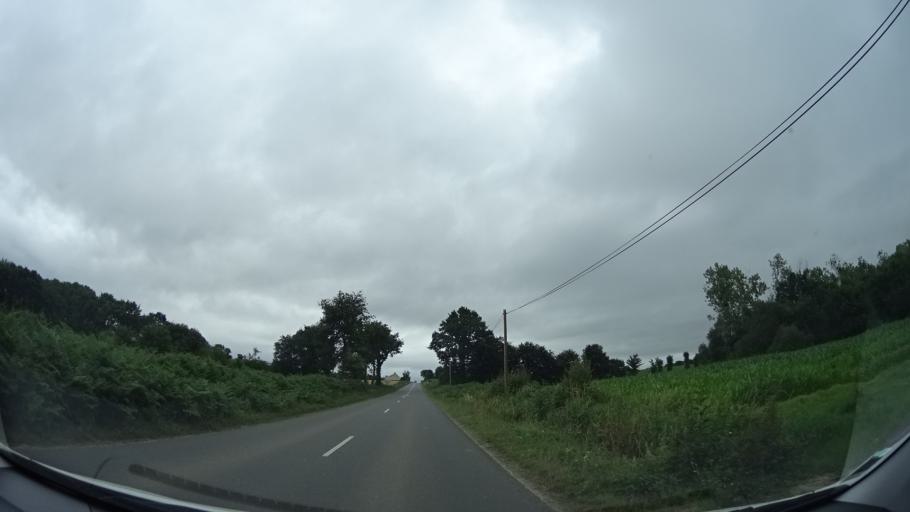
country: FR
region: Brittany
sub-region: Departement d'Ille-et-Vilaine
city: Meillac
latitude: 48.3927
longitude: -1.7929
